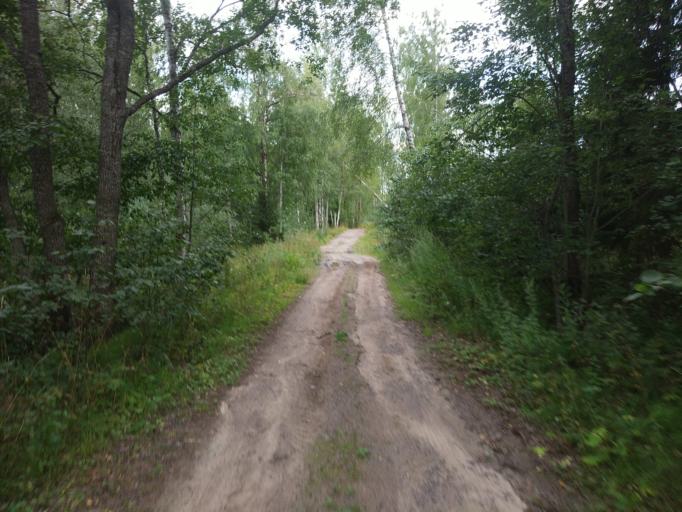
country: RU
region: Leningrad
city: Kuznechnoye
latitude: 61.1116
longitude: 29.6116
